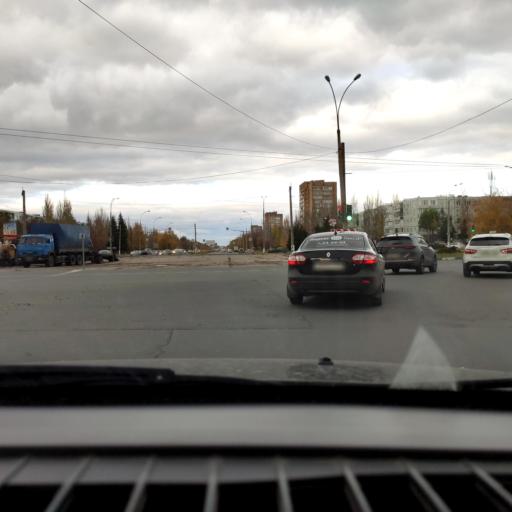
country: RU
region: Samara
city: Tol'yatti
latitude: 53.5268
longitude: 49.2969
